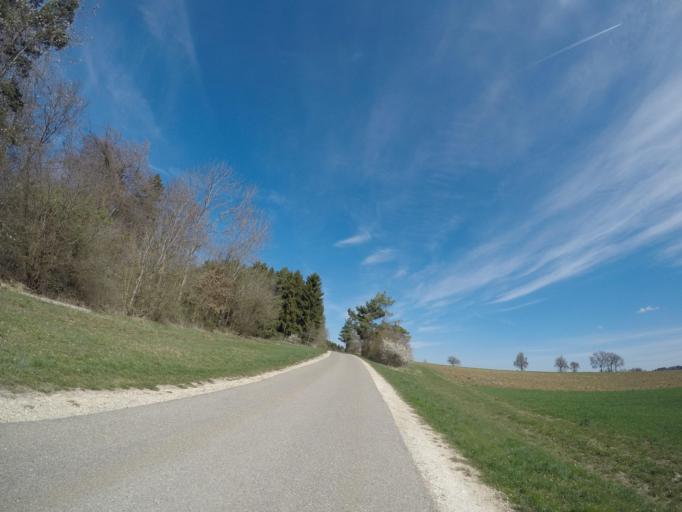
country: DE
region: Baden-Wuerttemberg
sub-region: Tuebingen Region
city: Mehrstetten
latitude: 48.3279
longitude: 9.5542
